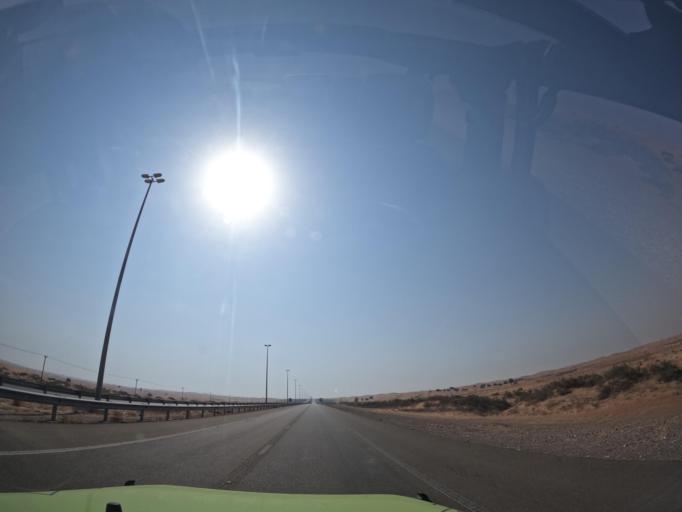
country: OM
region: Al Buraimi
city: Al Buraymi
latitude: 24.4572
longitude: 55.6445
